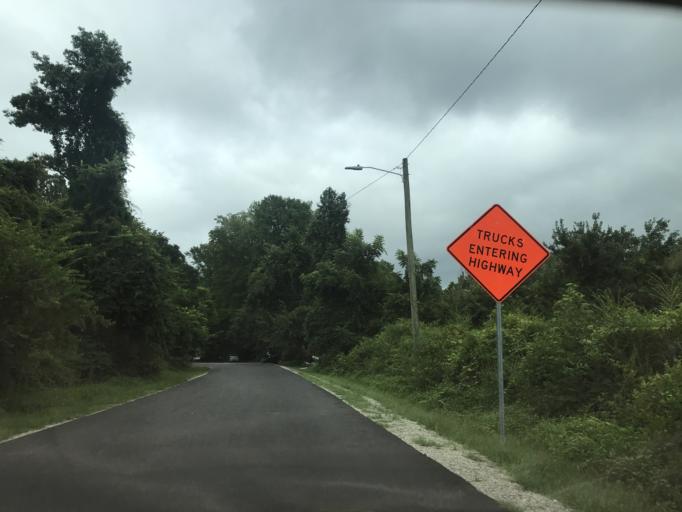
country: US
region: North Carolina
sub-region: Wake County
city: Knightdale
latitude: 35.7992
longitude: -78.5428
